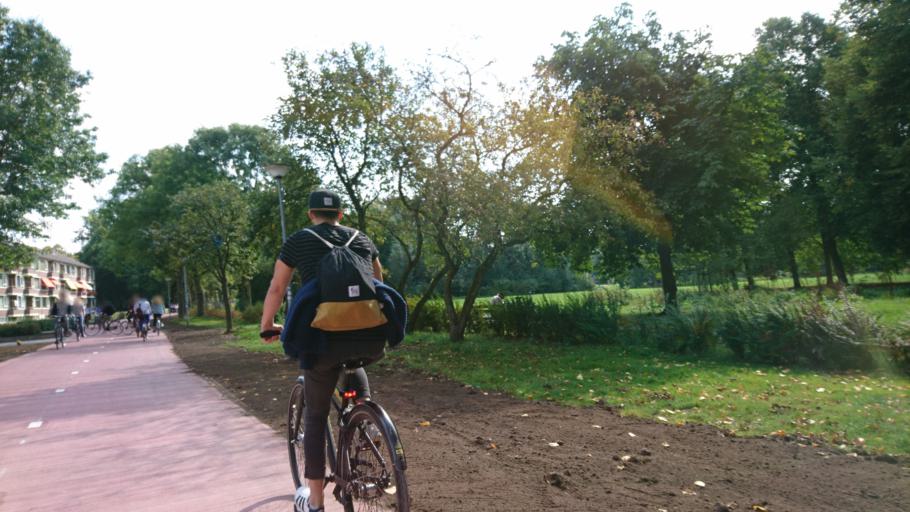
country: NL
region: Groningen
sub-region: Gemeente Groningen
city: Korrewegwijk
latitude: 53.2346
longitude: 6.5455
